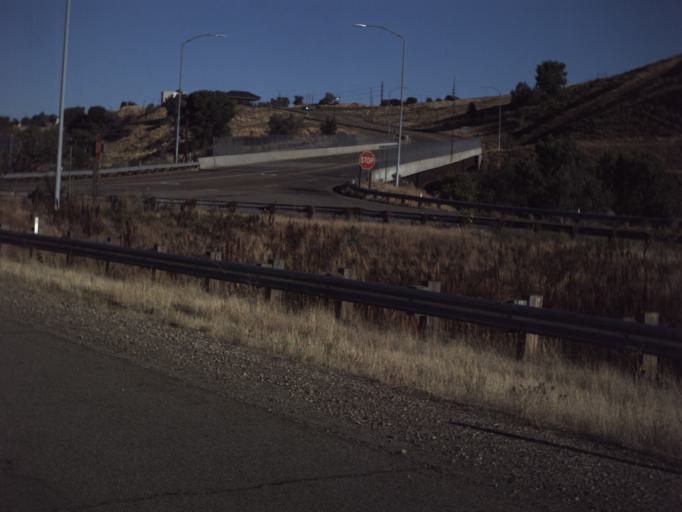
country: US
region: Utah
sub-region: Weber County
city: Washington Terrace
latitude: 41.1508
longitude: -111.9682
